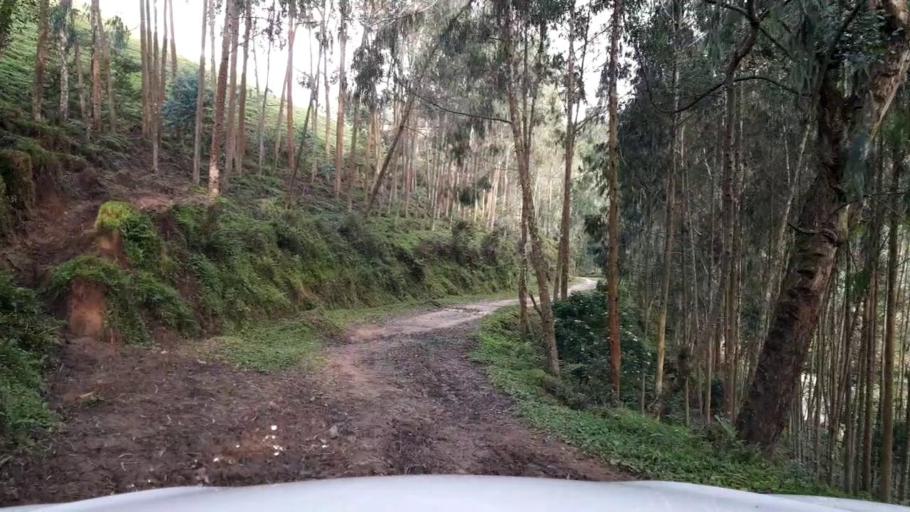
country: RW
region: Western Province
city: Gisenyi
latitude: -1.7239
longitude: 29.4349
